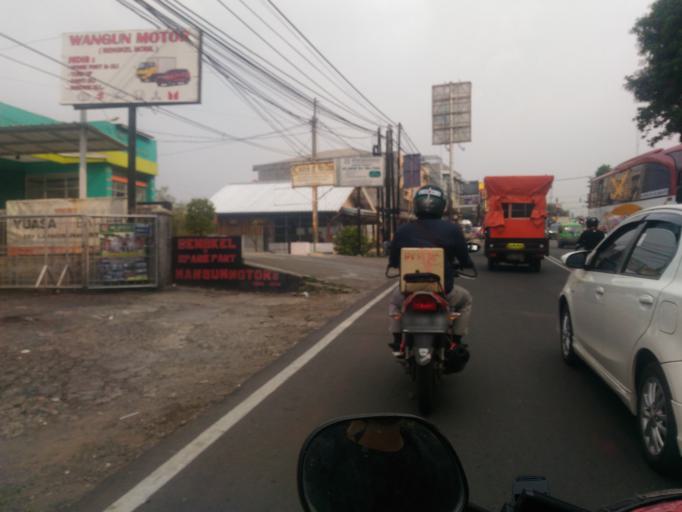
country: ID
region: West Java
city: Caringin
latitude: -6.6504
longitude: 106.8447
